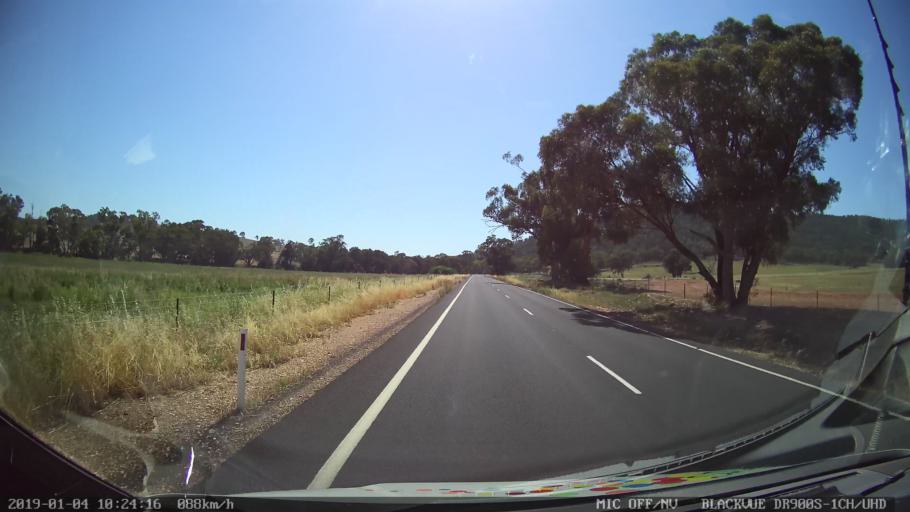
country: AU
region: New South Wales
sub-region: Cabonne
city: Canowindra
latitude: -33.3694
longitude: 148.5521
